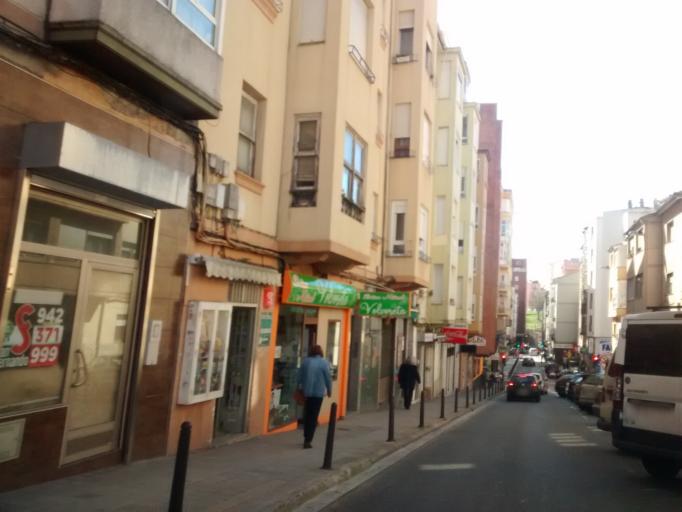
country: ES
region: Cantabria
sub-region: Provincia de Cantabria
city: Santander
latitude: 43.4644
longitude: -3.8110
